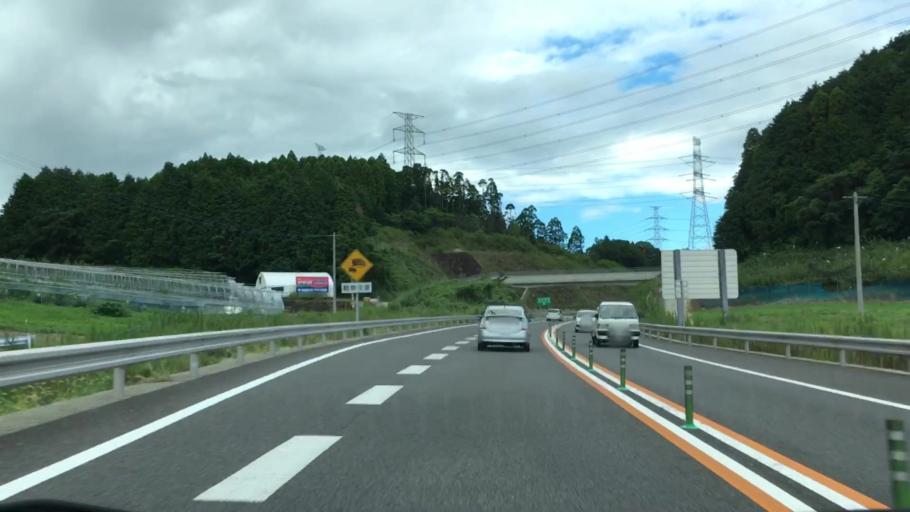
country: JP
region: Saga Prefecture
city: Imaricho-ko
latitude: 33.3500
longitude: 129.9244
